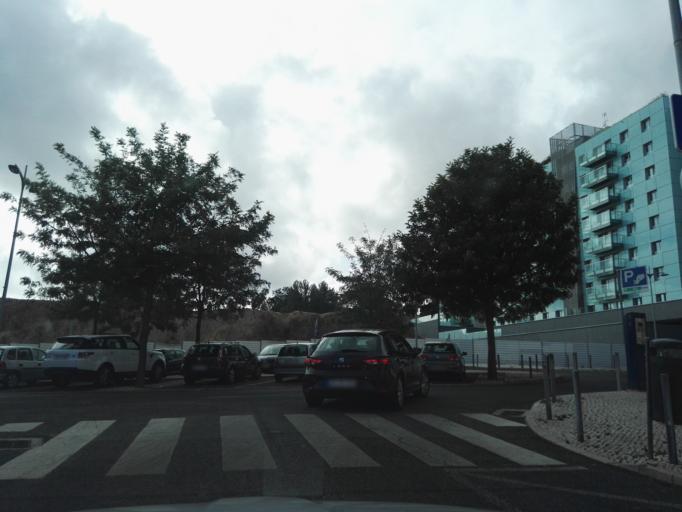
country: PT
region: Lisbon
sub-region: Lisbon
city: Lisbon
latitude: 38.7436
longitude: -9.1589
